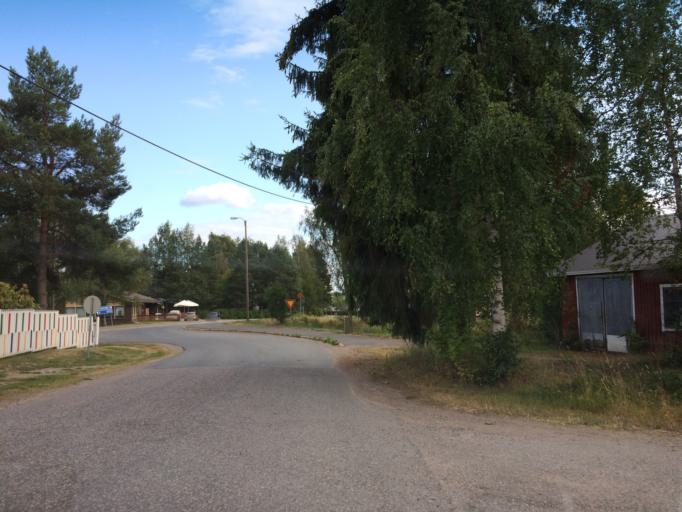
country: FI
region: Haeme
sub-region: Haemeenlinna
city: Tuulos
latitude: 61.0708
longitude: 24.6784
